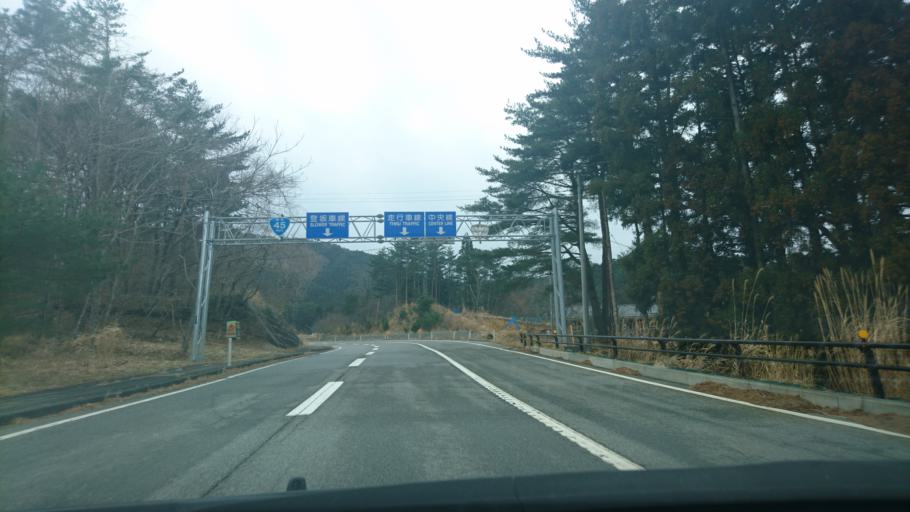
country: JP
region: Iwate
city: Ofunato
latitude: 39.1385
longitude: 141.8246
